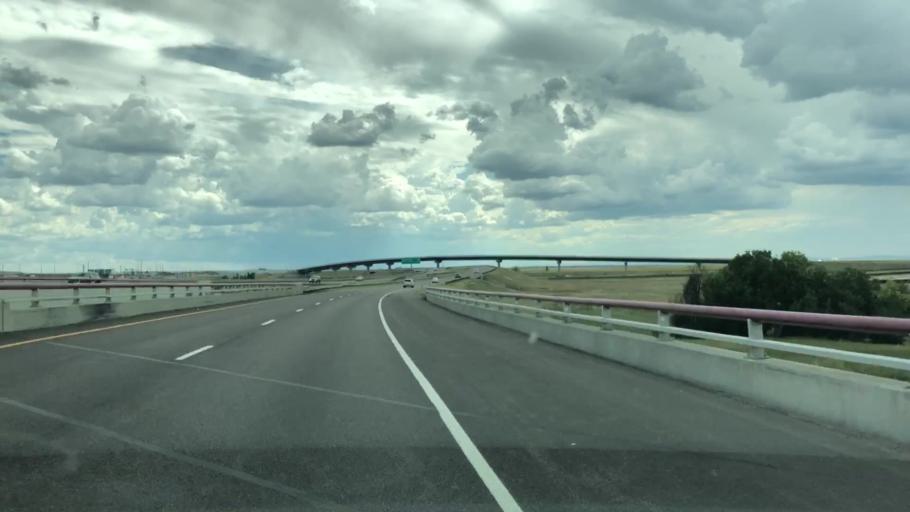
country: US
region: Colorado
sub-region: Adams County
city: Aurora
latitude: 39.7458
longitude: -104.7169
